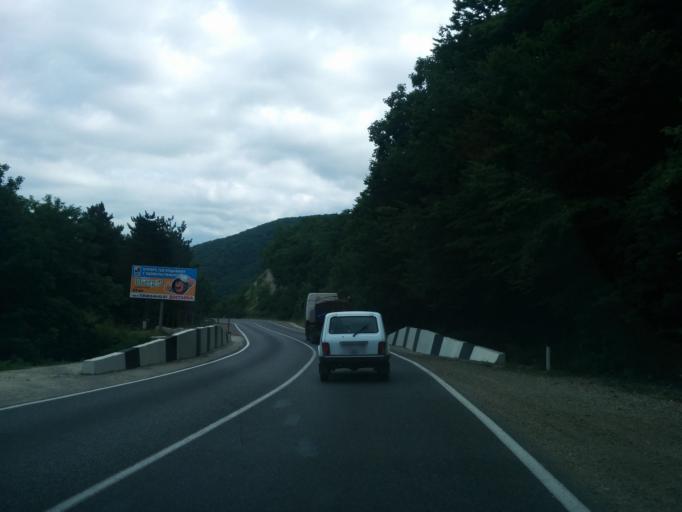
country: RU
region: Krasnodarskiy
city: Agoy
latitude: 44.1343
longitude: 39.0511
